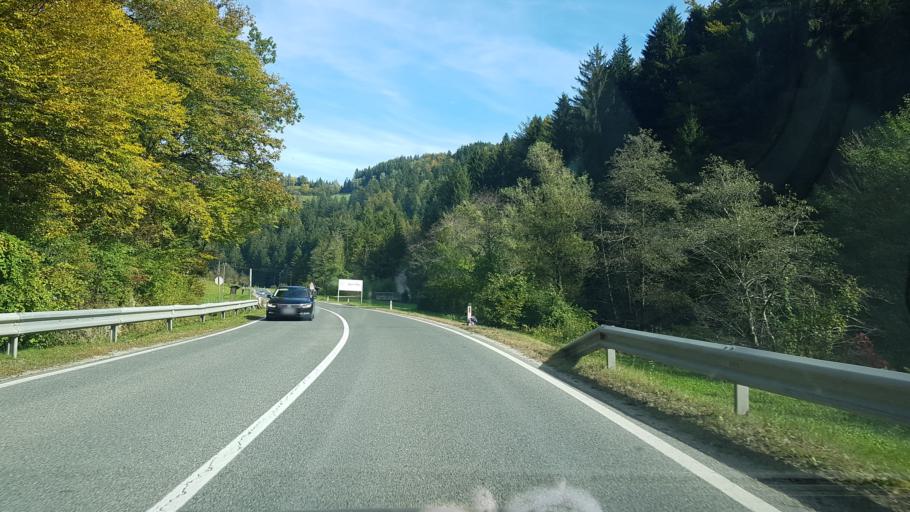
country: SI
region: Velenje
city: Velenje
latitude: 46.3960
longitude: 15.1717
